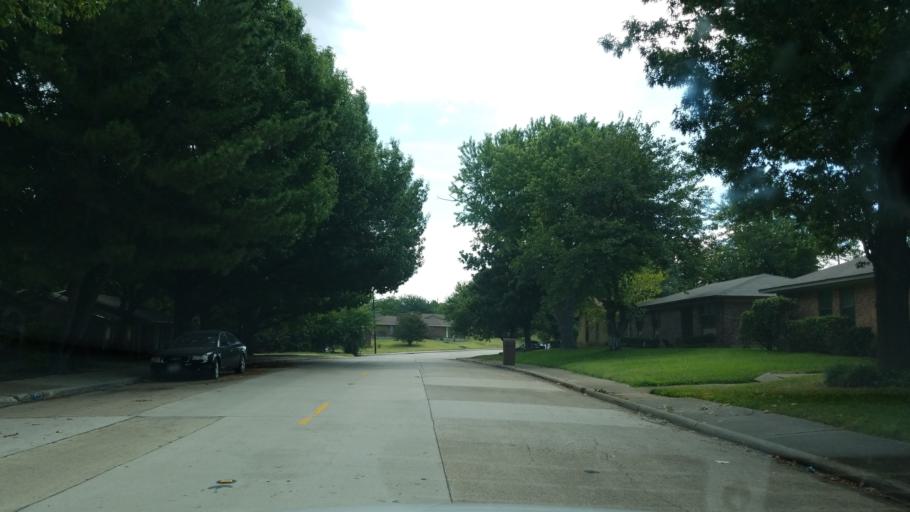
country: US
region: Texas
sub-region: Dallas County
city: Duncanville
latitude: 32.6545
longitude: -96.8428
